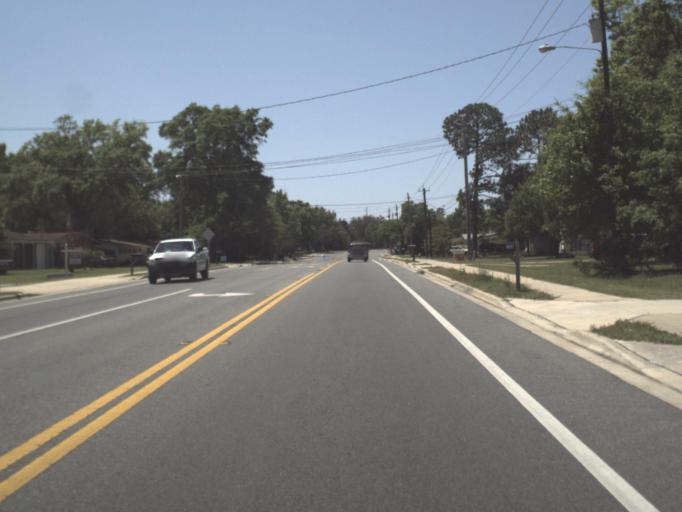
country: US
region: Florida
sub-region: Escambia County
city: Ferry Pass
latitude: 30.4977
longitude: -87.1824
